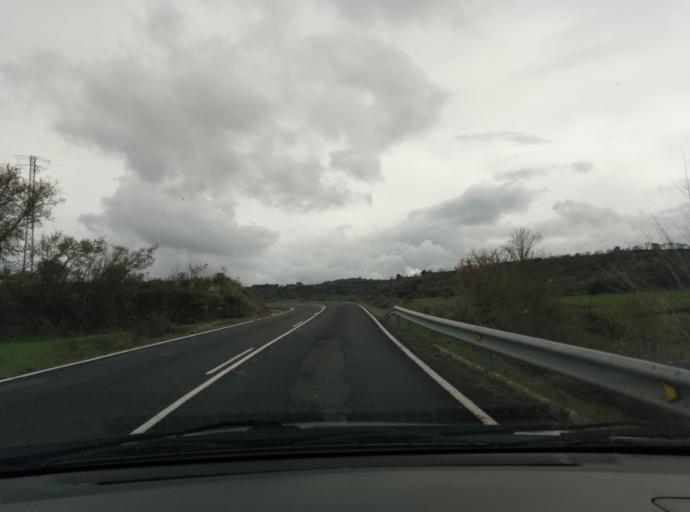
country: ES
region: Catalonia
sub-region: Provincia de Lleida
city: Cervera
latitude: 41.6200
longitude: 1.3388
